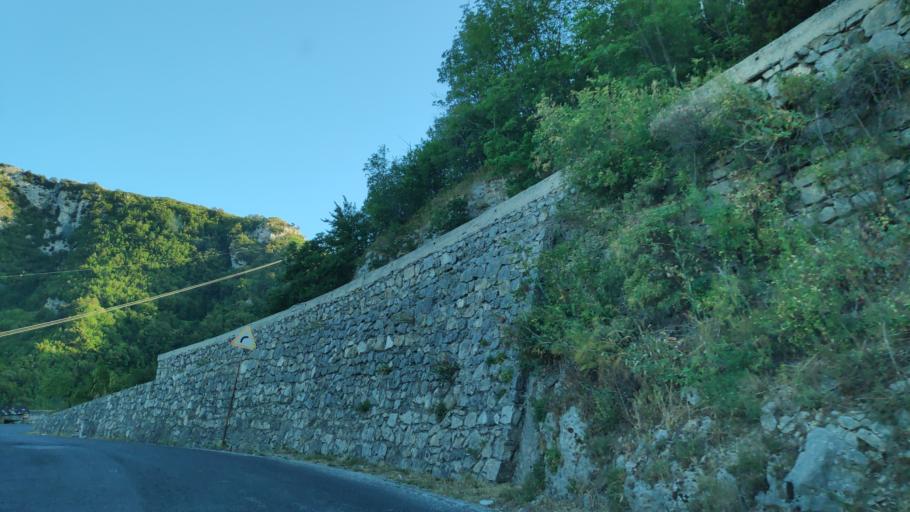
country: IT
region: Campania
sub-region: Provincia di Salerno
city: Corbara
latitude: 40.7236
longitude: 14.6062
